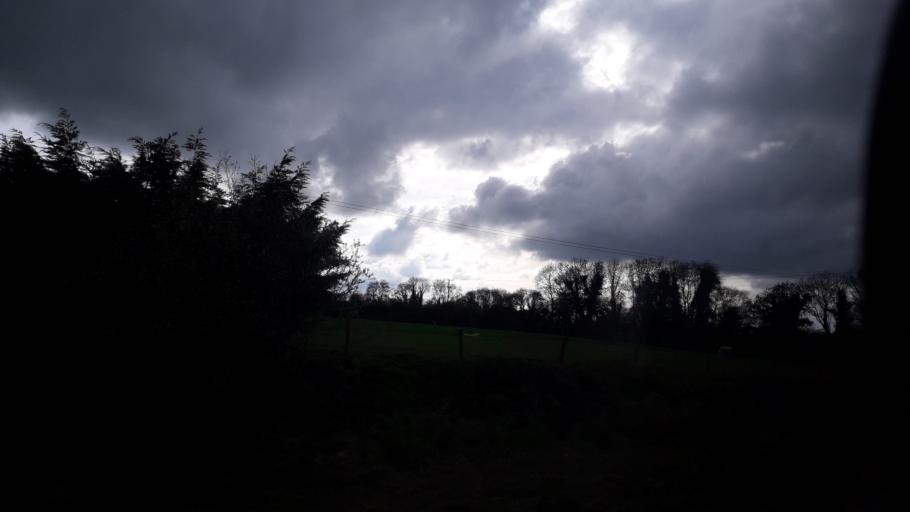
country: IE
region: Leinster
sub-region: An Iarmhi
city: Rathwire
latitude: 53.4938
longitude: -7.1593
